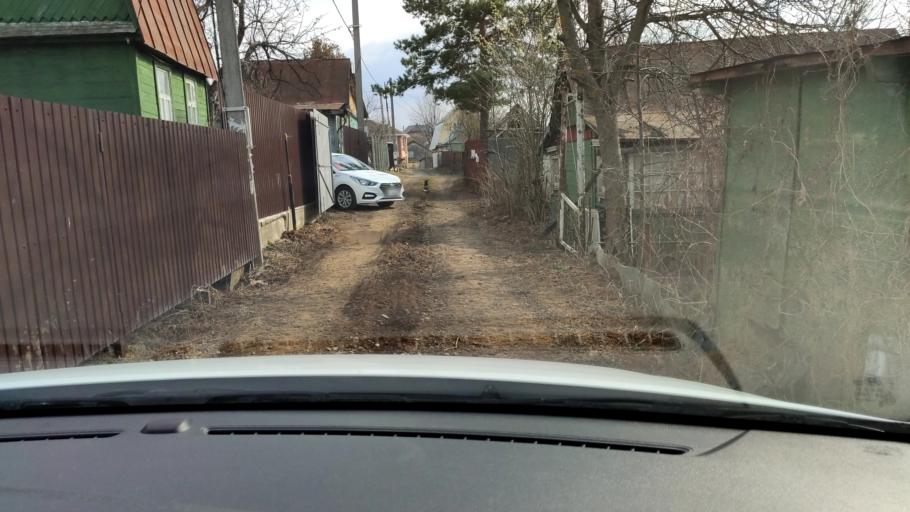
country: RU
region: Tatarstan
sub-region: Gorod Kazan'
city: Kazan
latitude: 55.8192
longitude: 49.2115
